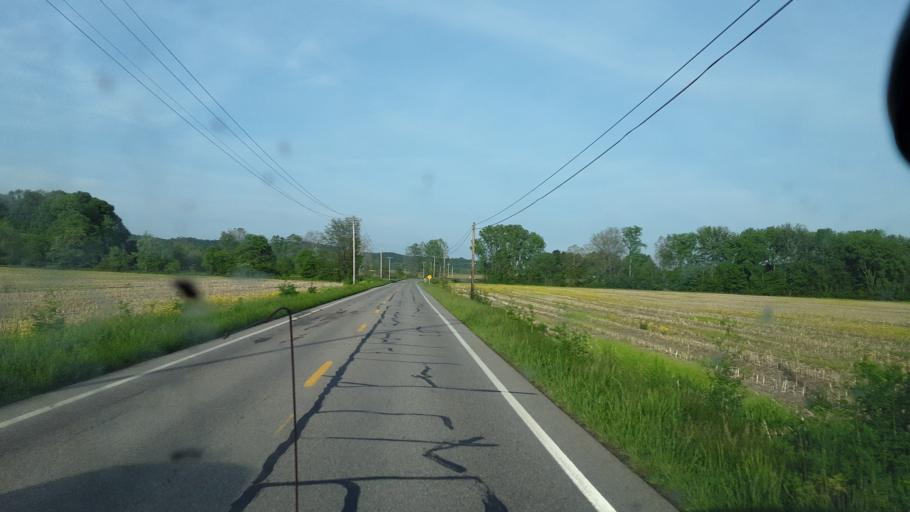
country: US
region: Ohio
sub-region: Ross County
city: Kingston
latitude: 39.4970
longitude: -82.7075
